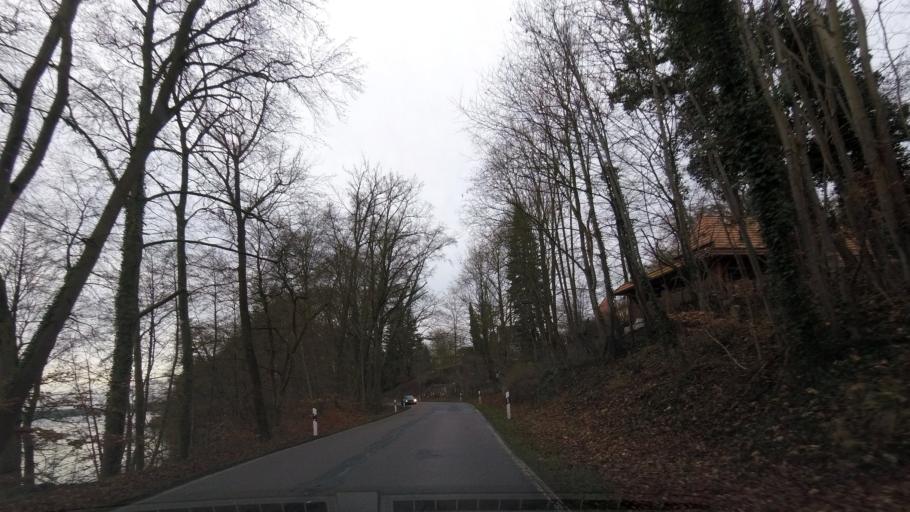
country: DE
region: Mecklenburg-Vorpommern
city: Waren
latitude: 53.5393
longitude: 12.6875
